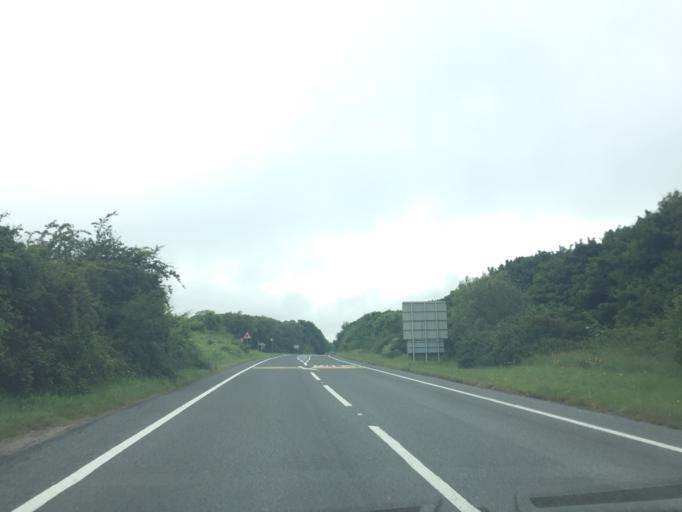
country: GB
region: England
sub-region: Dorset
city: Wareham
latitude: 50.6450
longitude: -2.0669
